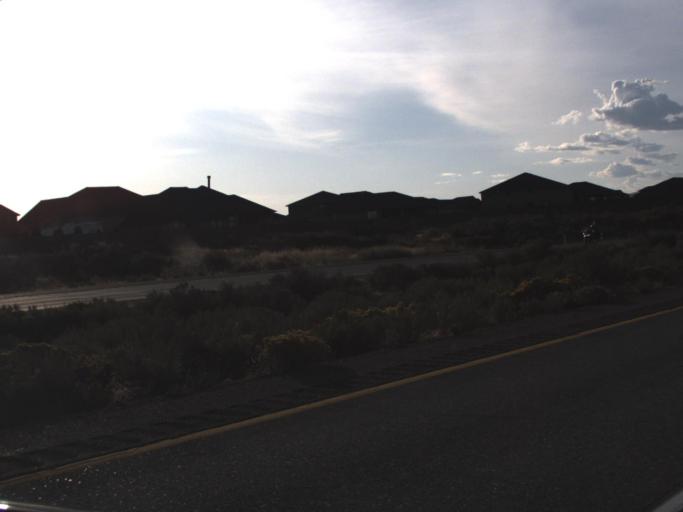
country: US
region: Washington
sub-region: Benton County
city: Richland
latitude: 46.2037
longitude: -119.3327
